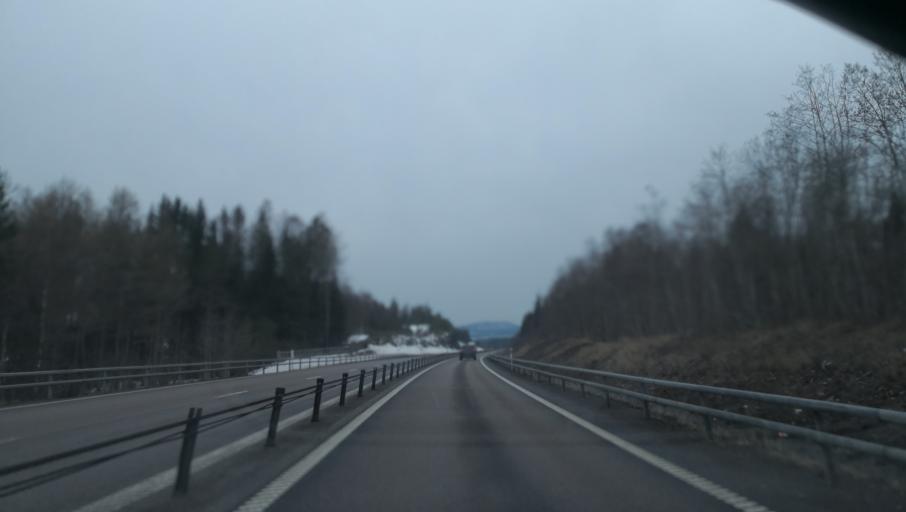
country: SE
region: Vaesternorrland
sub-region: Haernoesands Kommun
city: Haernoesand
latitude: 62.7119
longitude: 17.8981
